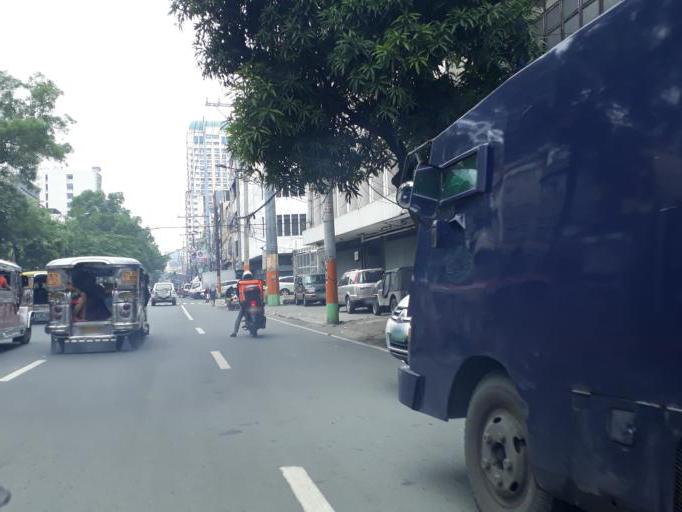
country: PH
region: Metro Manila
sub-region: City of Manila
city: Manila
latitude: 14.6160
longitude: 120.9771
